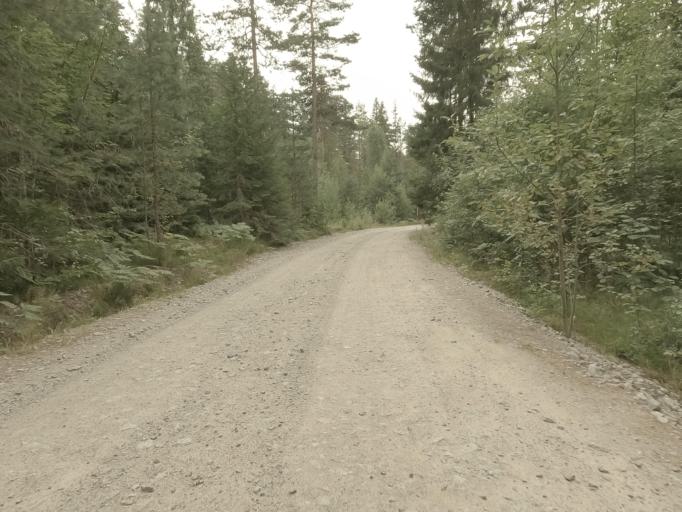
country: RU
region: Leningrad
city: Kamennogorsk
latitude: 60.9867
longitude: 29.1832
